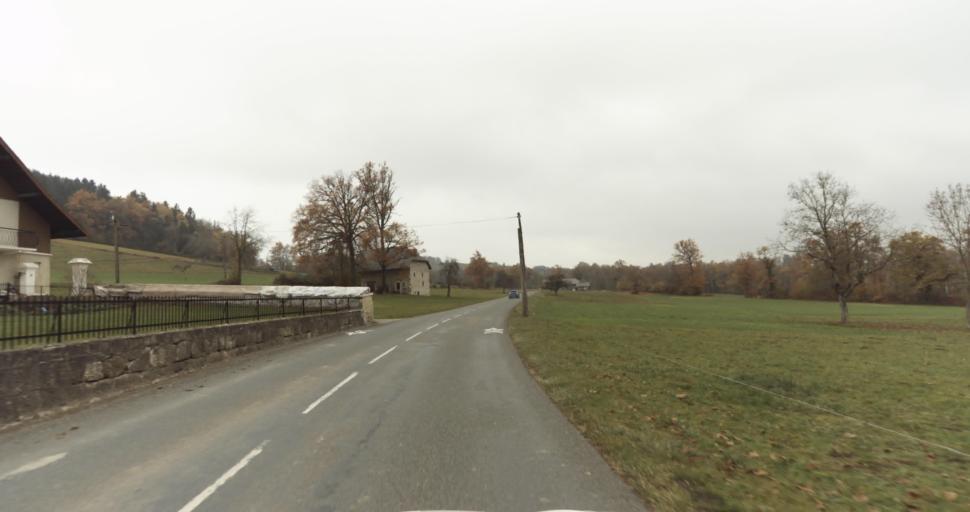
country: FR
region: Rhone-Alpes
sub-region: Departement de la Haute-Savoie
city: Cusy
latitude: 45.7867
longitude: 6.0128
